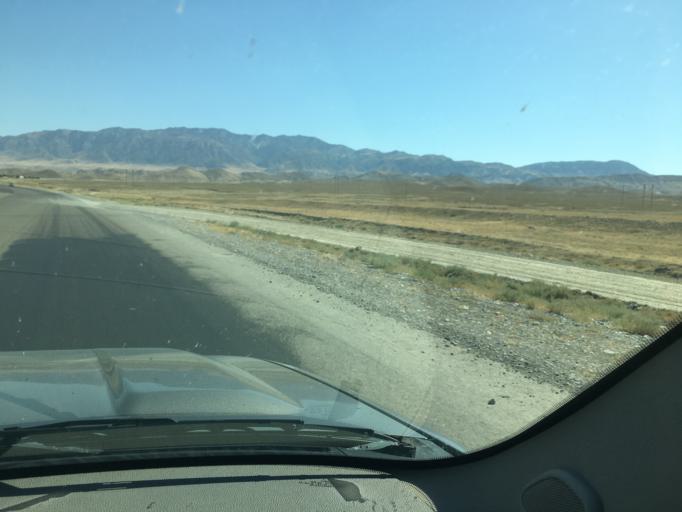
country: TM
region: Balkan
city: Serdar
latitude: 38.7385
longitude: 56.7723
